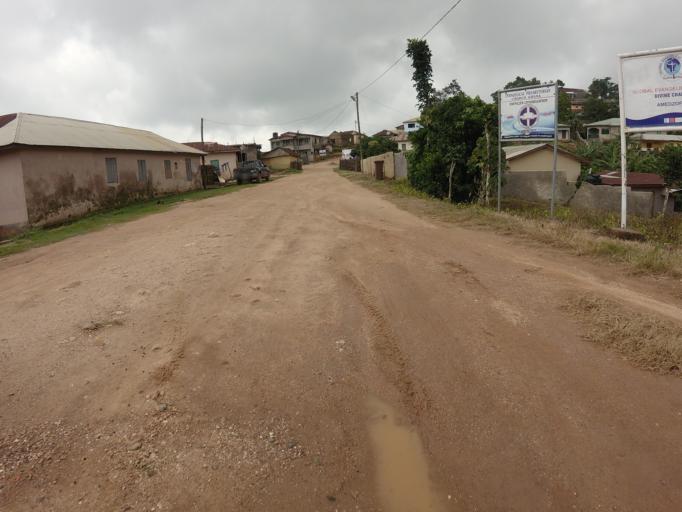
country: TG
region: Plateaux
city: Kpalime
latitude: 6.8436
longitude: 0.4348
